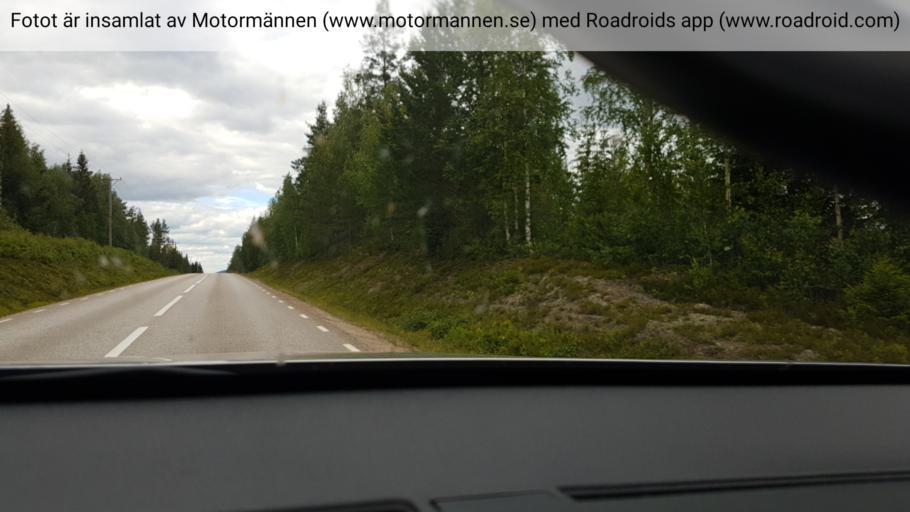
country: NO
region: Hedmark
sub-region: Trysil
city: Innbygda
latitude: 61.0002
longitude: 12.4841
